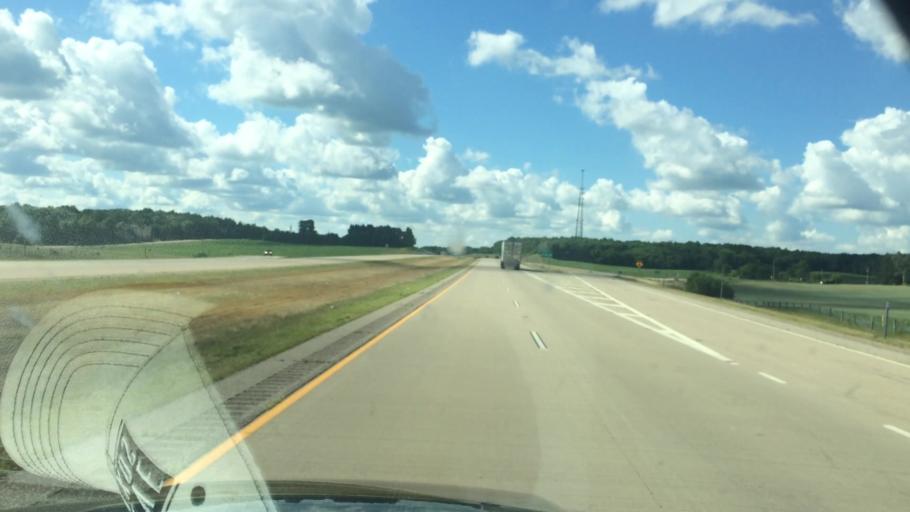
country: US
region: Wisconsin
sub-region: Portage County
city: Amherst
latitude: 44.4573
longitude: -89.3127
